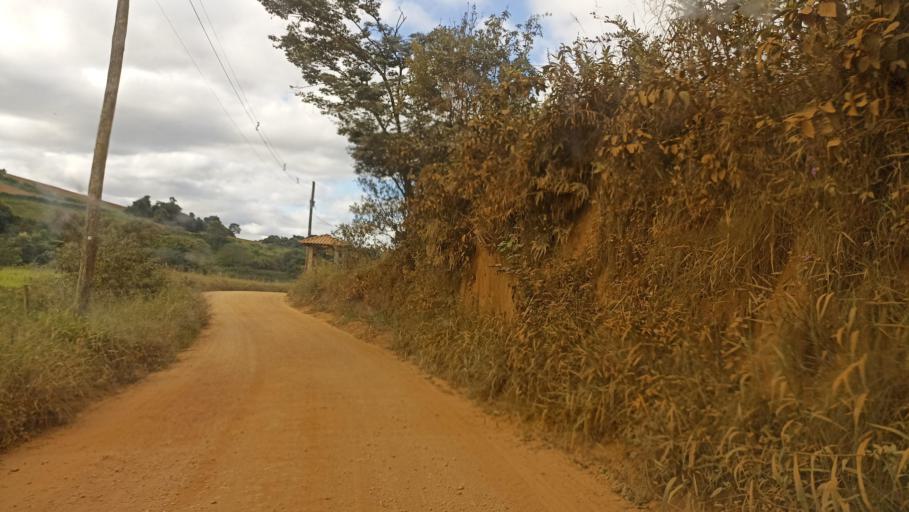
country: BR
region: Minas Gerais
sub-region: Tiradentes
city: Tiradentes
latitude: -21.0971
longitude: -44.0762
